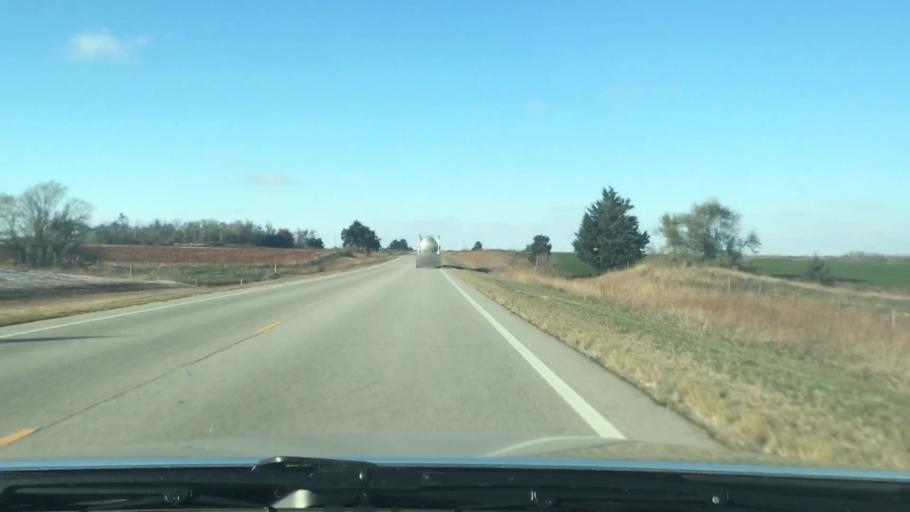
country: US
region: Kansas
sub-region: Rice County
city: Sterling
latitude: 38.1496
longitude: -98.2040
